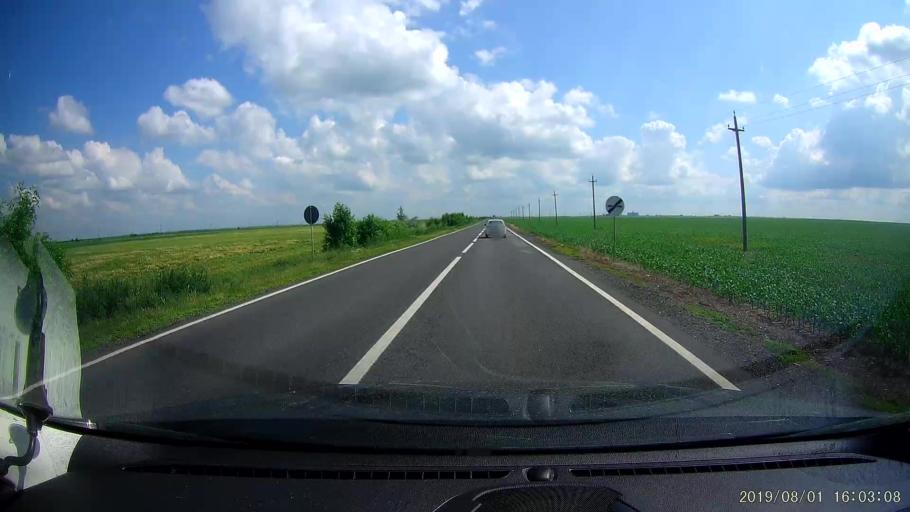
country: RO
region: Calarasi
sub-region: Comuna Dragalina
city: Drajna Noua
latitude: 44.4780
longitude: 27.3854
